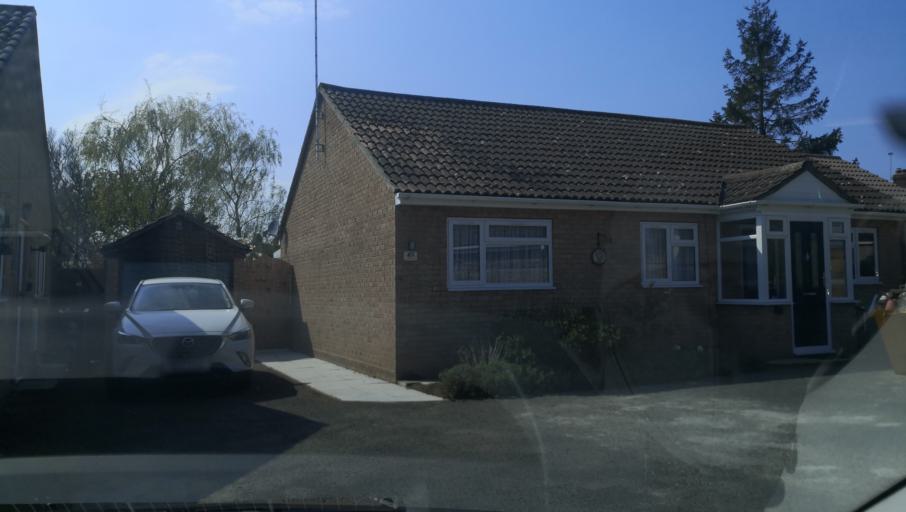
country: GB
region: England
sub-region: Essex
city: Little Clacton
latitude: 51.8585
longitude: 1.1687
